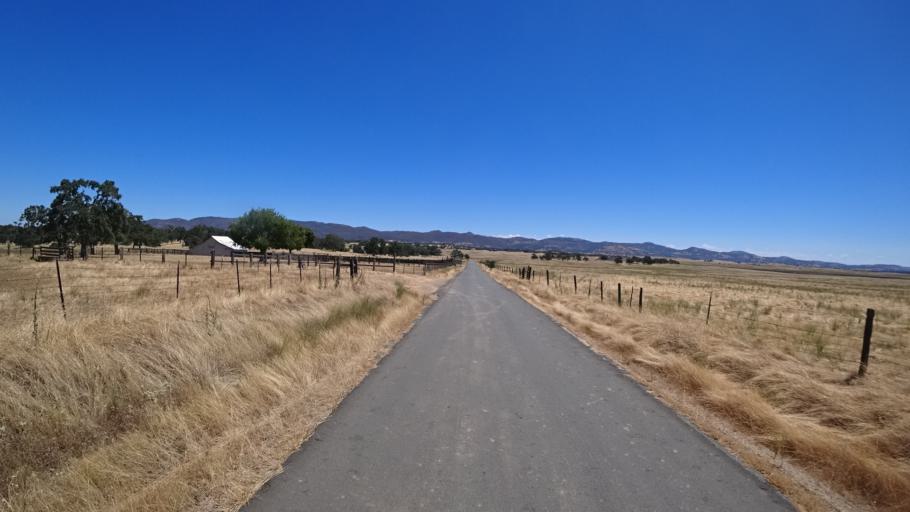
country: US
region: California
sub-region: Calaveras County
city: Rancho Calaveras
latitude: 38.0557
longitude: -120.7785
